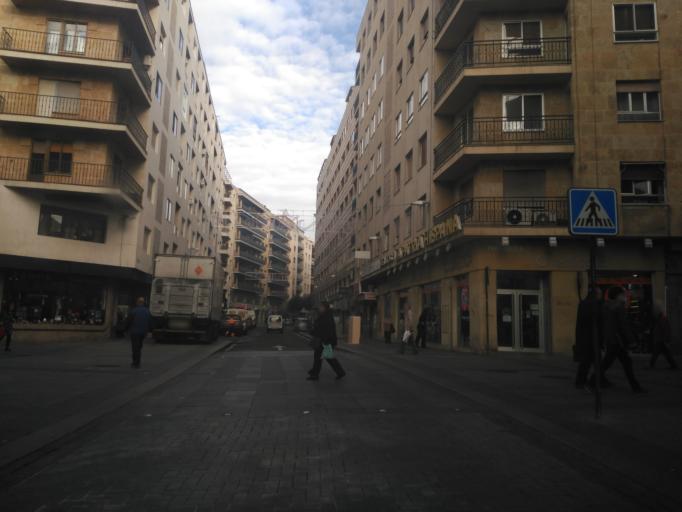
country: ES
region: Castille and Leon
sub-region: Provincia de Salamanca
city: Salamanca
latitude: 40.9649
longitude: -5.6657
